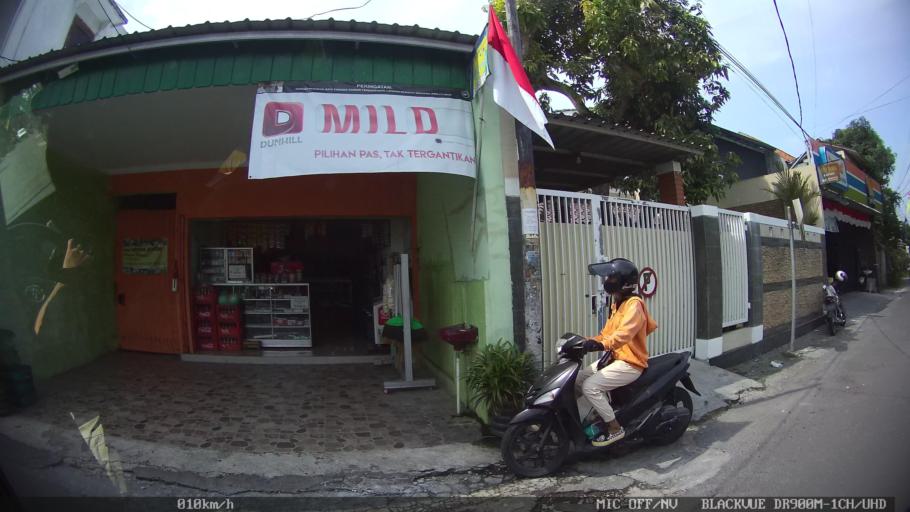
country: ID
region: Daerah Istimewa Yogyakarta
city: Depok
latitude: -7.7851
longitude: 110.4062
